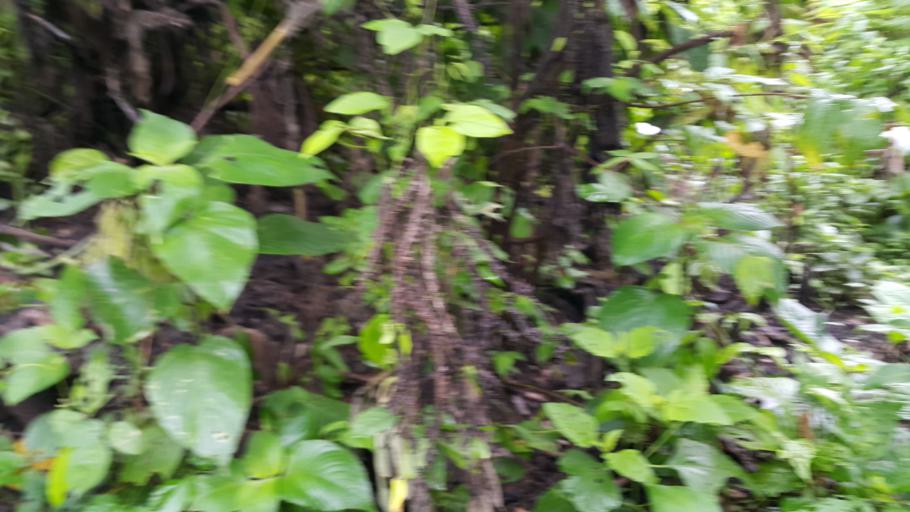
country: NI
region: Chinandega
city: Jiquilillo
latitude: 12.9739
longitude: -87.5516
